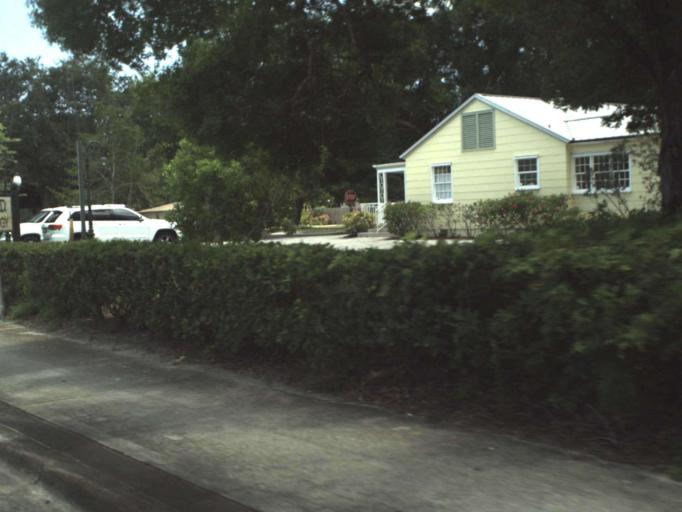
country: US
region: Florida
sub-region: Indian River County
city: Vero Beach
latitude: 27.6381
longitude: -80.4086
